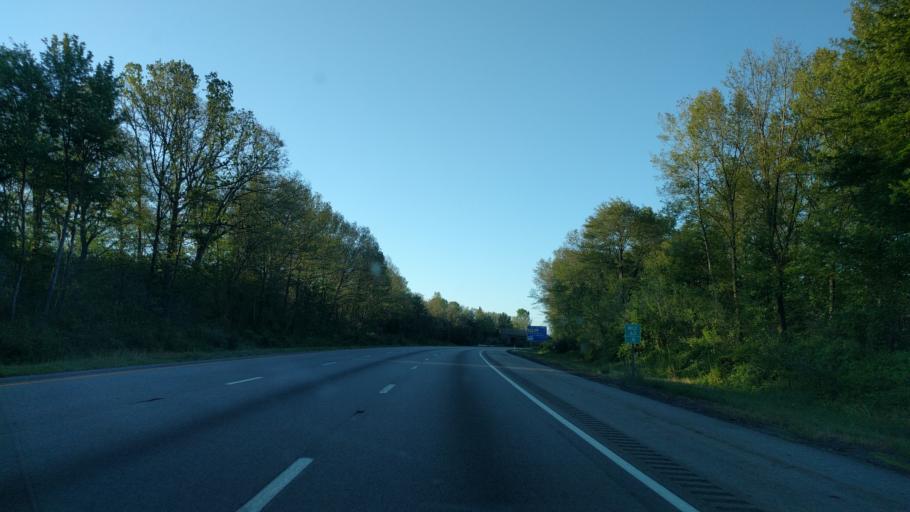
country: US
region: Massachusetts
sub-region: Middlesex County
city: Marlborough
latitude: 42.3504
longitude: -71.5778
